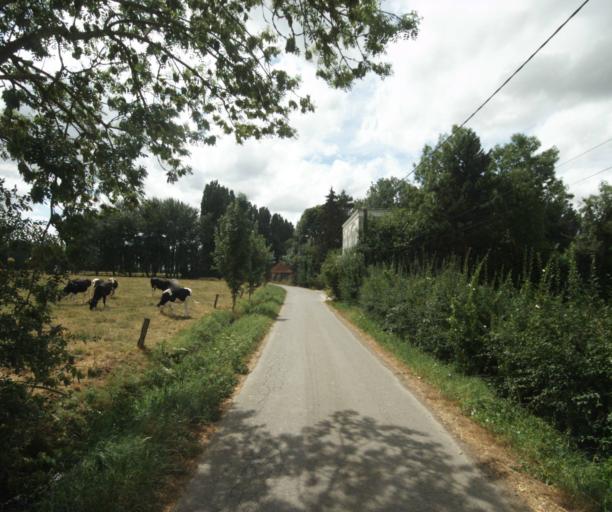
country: FR
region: Nord-Pas-de-Calais
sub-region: Departement du Nord
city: Linselles
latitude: 50.7527
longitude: 3.0656
